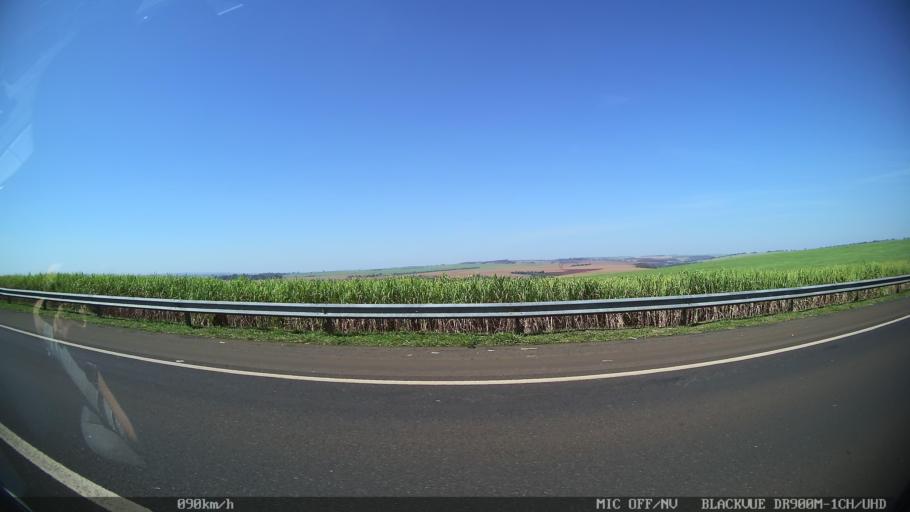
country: BR
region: Sao Paulo
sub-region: Batatais
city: Batatais
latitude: -20.7708
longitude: -47.5406
